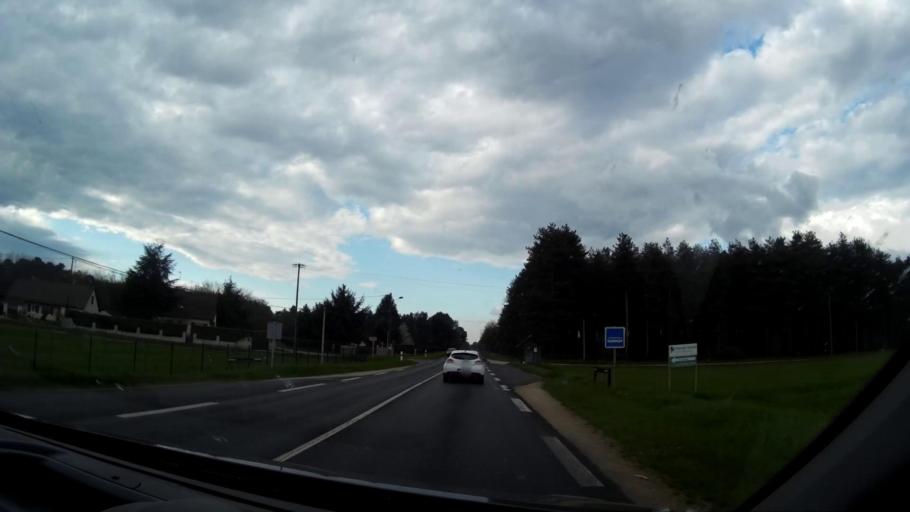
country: FR
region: Centre
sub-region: Departement du Loir-et-Cher
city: Contres
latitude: 47.4542
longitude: 1.4257
